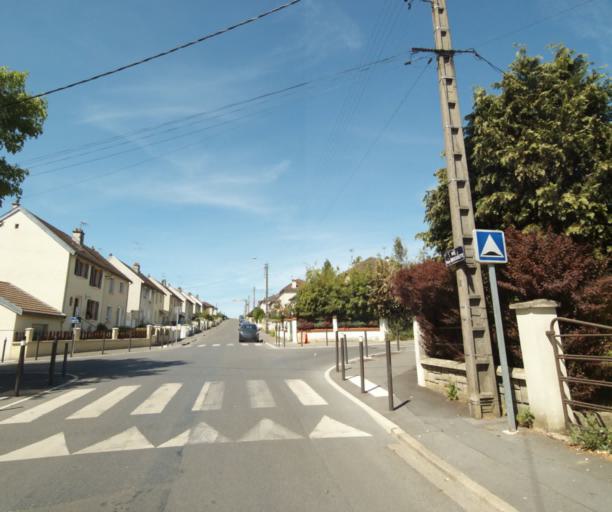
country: FR
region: Champagne-Ardenne
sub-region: Departement des Ardennes
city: Charleville-Mezieres
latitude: 49.7489
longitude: 4.7180
